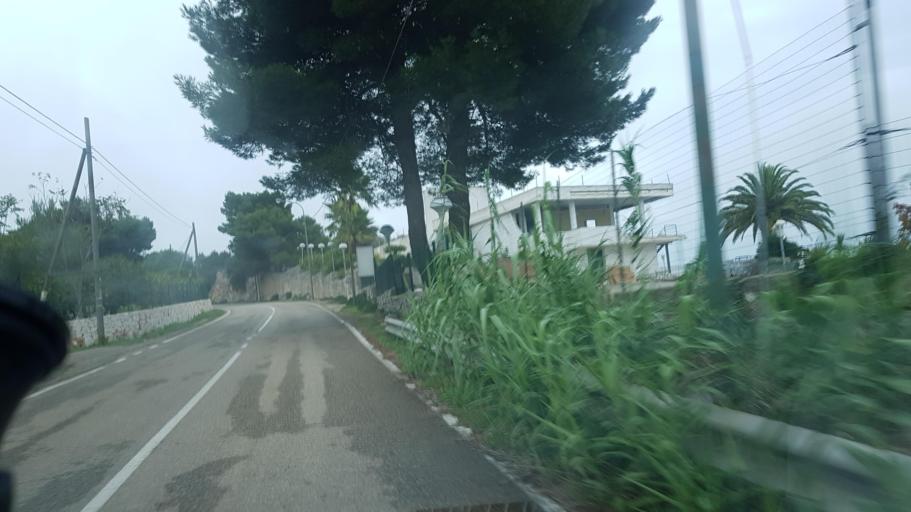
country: IT
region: Apulia
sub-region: Provincia di Brindisi
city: Ostuni
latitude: 40.7342
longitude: 17.5535
